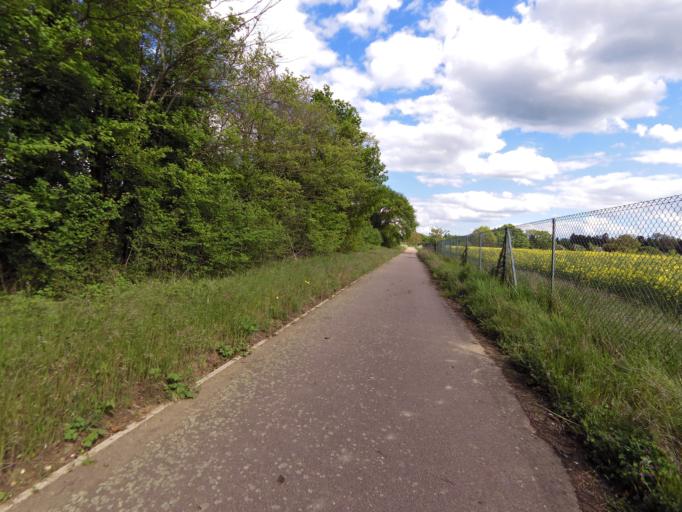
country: GB
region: England
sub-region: Suffolk
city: Great Barton
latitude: 52.2482
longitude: 0.7781
